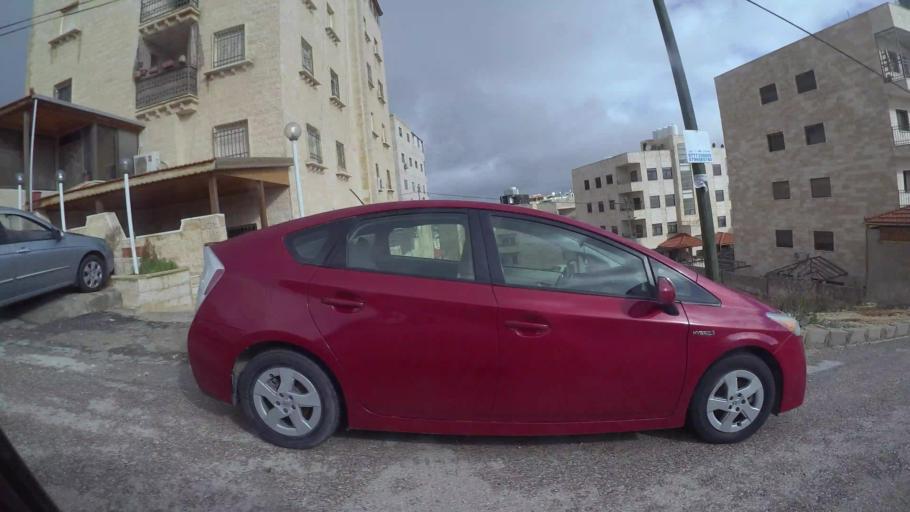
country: JO
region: Amman
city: Al Jubayhah
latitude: 32.0618
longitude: 35.8895
